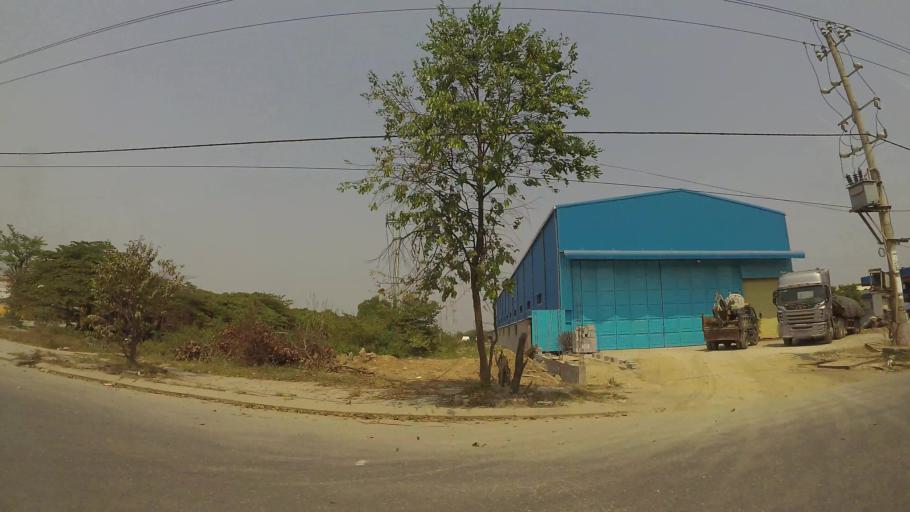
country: VN
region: Da Nang
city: Cam Le
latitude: 15.9867
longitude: 108.2009
